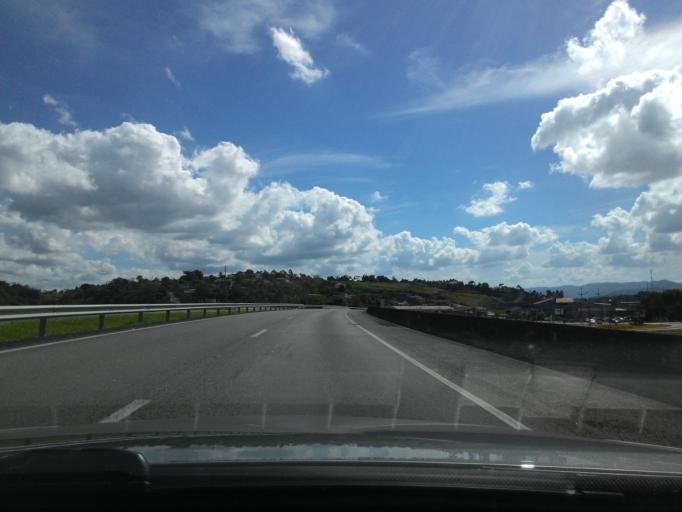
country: BR
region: Sao Paulo
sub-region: Cajati
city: Cajati
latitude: -24.7304
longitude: -48.0972
